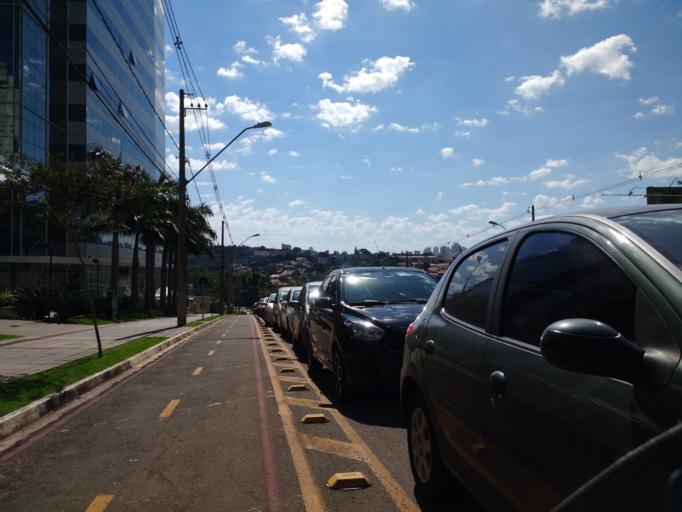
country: BR
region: Parana
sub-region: Londrina
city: Londrina
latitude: -23.3280
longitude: -51.1774
